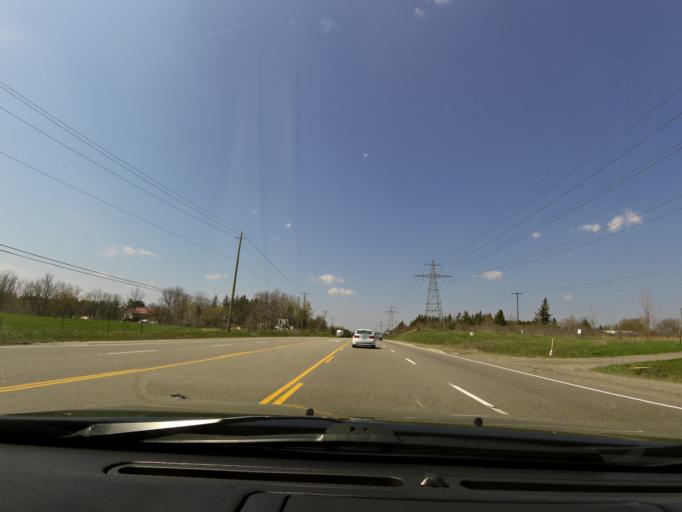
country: CA
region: Ontario
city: Ancaster
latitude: 43.3827
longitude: -80.0141
